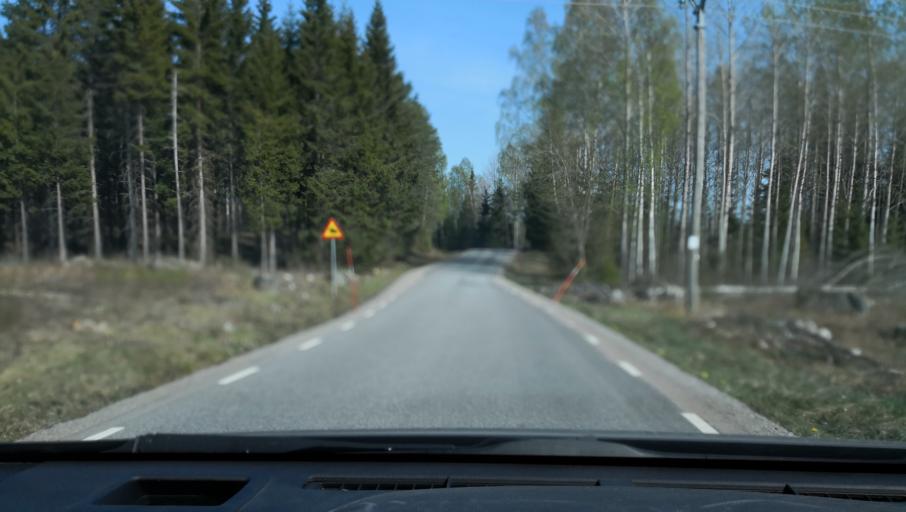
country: SE
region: Vaestmanland
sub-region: Sala Kommun
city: Sala
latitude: 59.9976
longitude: 16.6552
